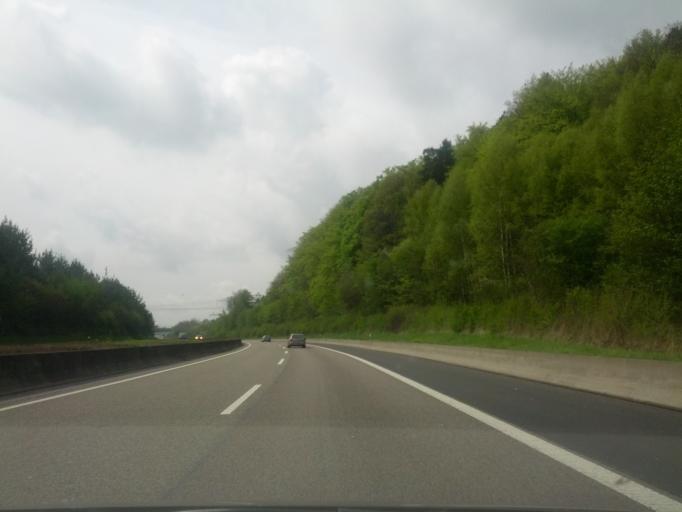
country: DE
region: Thuringia
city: Gerstungen
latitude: 51.0035
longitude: 10.0922
